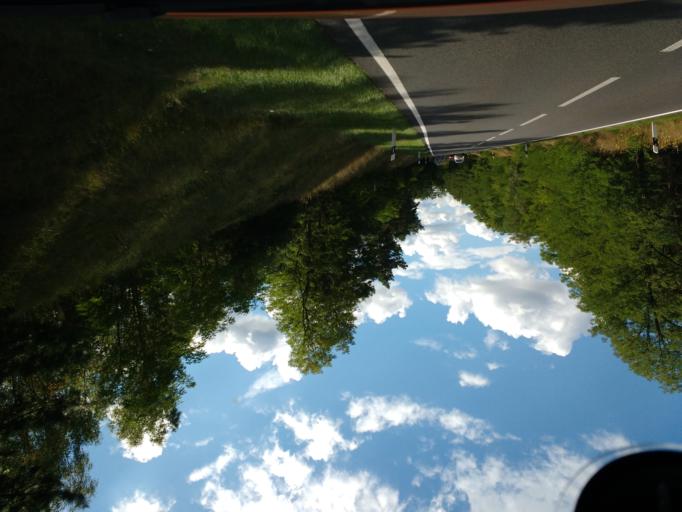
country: DE
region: Brandenburg
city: Wendisch Rietz
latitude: 52.2196
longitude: 13.9810
